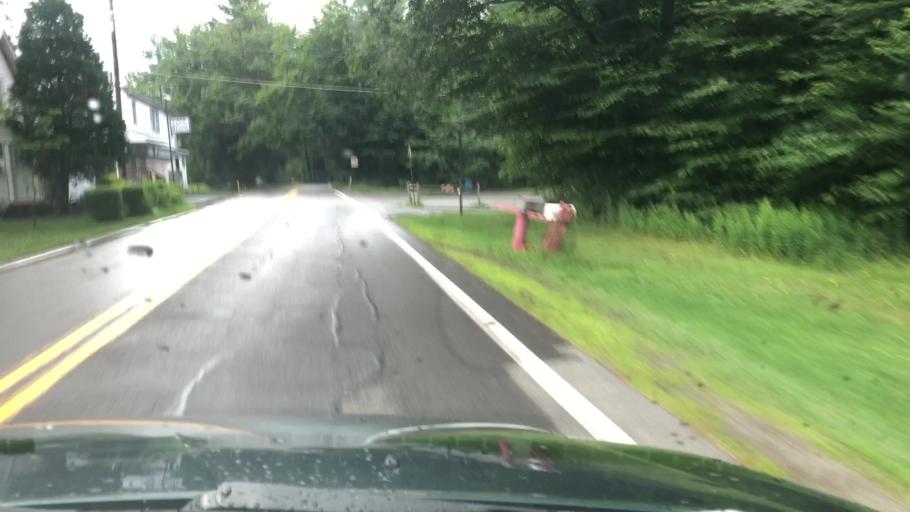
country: US
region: Pennsylvania
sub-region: Monroe County
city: Mountainhome
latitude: 41.3142
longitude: -75.2104
